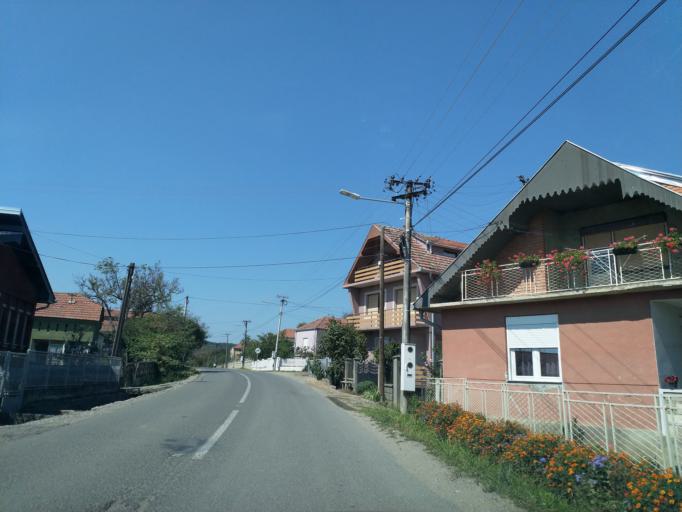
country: RS
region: Central Serbia
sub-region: Rasinski Okrug
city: Krusevac
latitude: 43.6242
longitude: 21.3430
